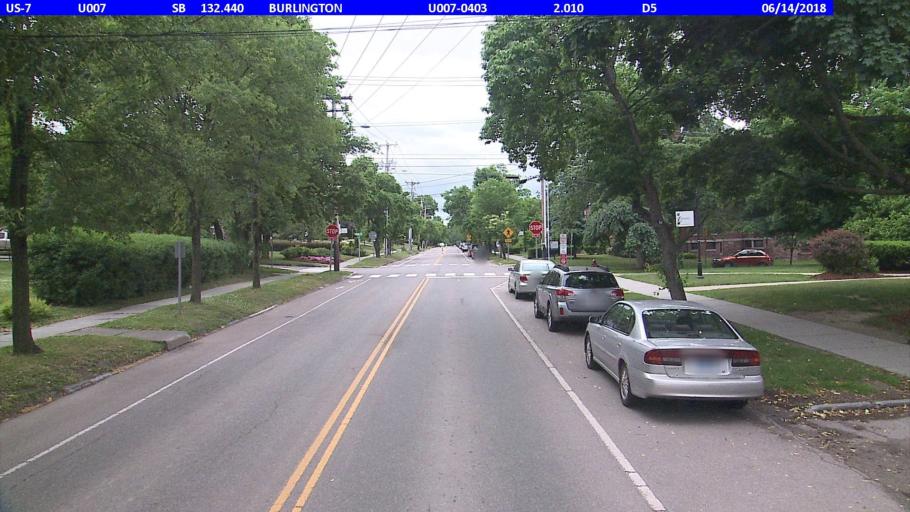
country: US
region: Vermont
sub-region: Chittenden County
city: Burlington
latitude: 44.4744
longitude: -73.2054
